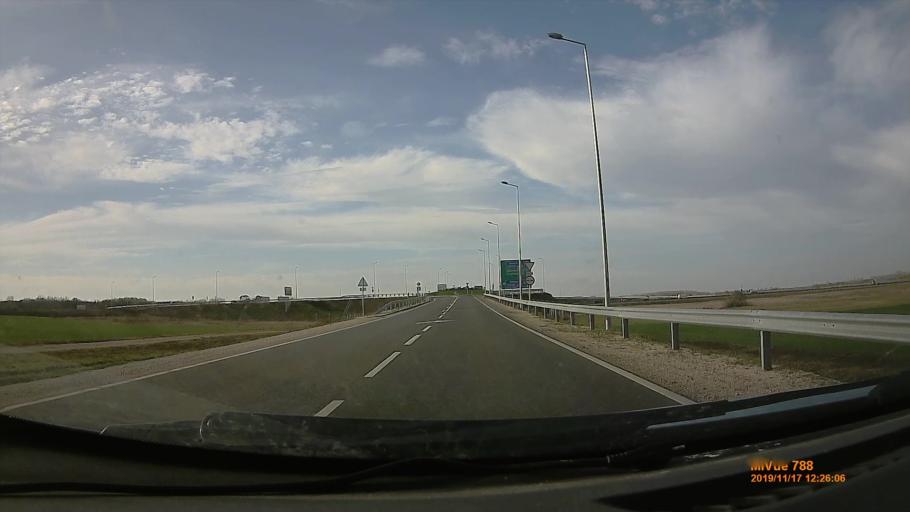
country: HU
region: Bacs-Kiskun
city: Kecskemet
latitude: 46.9323
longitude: 19.6218
